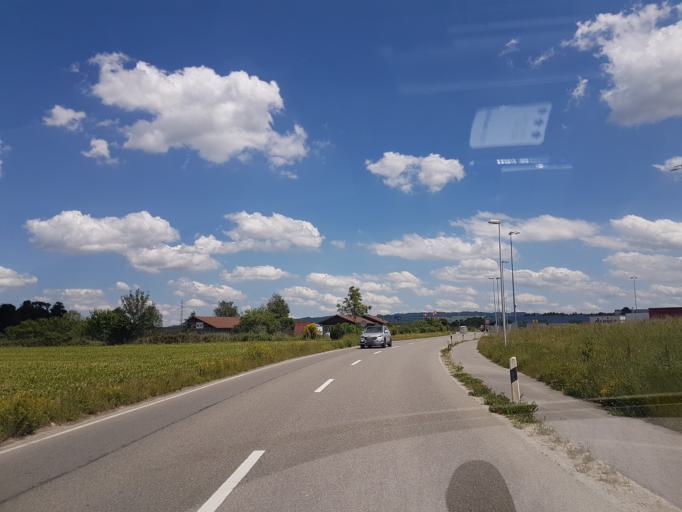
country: CH
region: Aargau
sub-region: Bezirk Lenzburg
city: Othmarsingen
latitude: 47.4157
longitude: 8.2276
